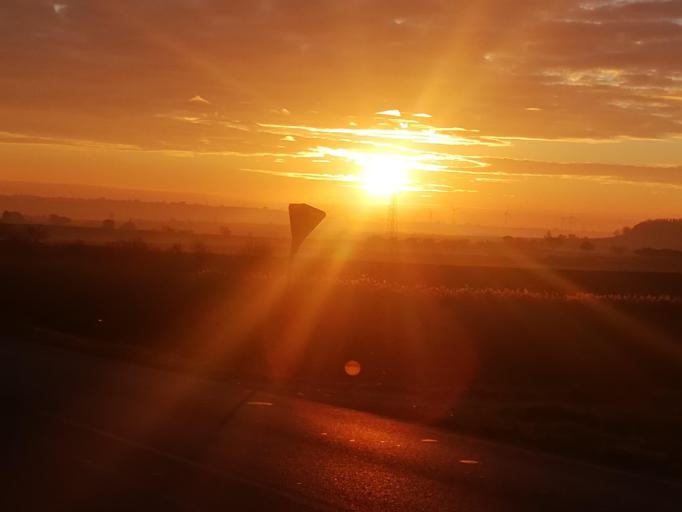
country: IT
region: Apulia
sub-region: Provincia di Bari
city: Altamura
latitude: 40.8182
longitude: 16.5501
